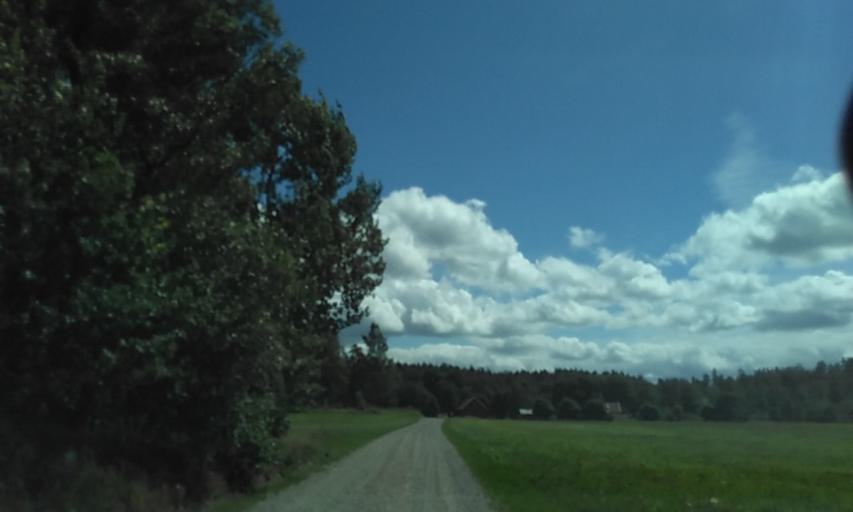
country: SE
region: Vaestra Goetaland
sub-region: Vargarda Kommun
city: Vargarda
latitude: 58.0478
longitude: 12.8414
